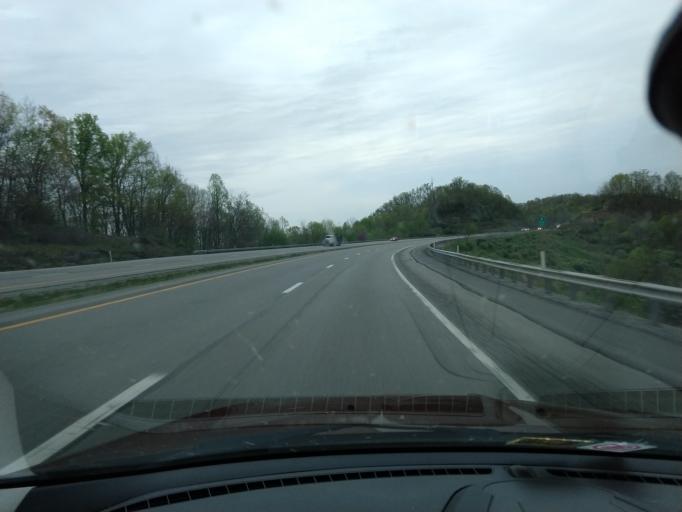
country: US
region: West Virginia
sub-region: Lewis County
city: Weston
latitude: 38.9428
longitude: -80.5412
